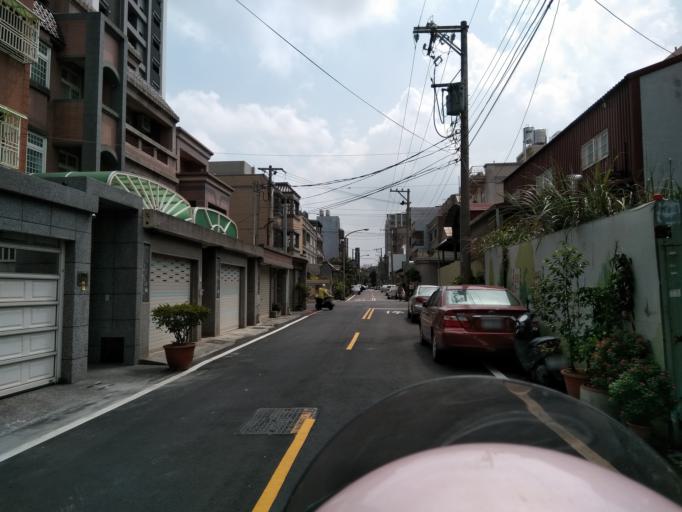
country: TW
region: Taiwan
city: Taoyuan City
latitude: 25.0231
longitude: 121.2619
